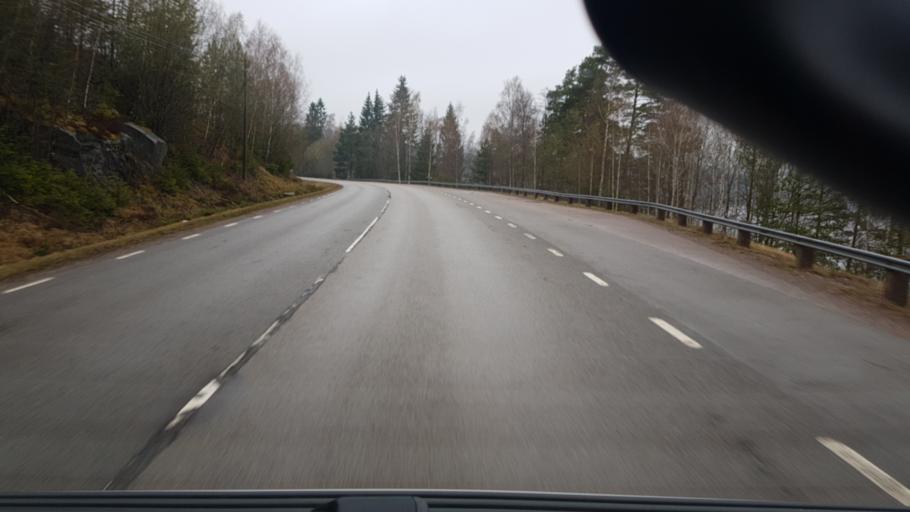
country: SE
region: Vaermland
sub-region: Arvika Kommun
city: Arvika
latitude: 59.7100
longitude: 12.6357
